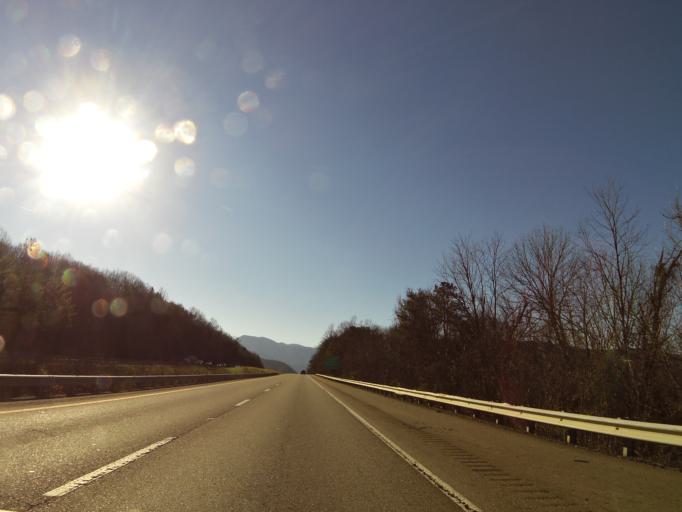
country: US
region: Tennessee
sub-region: Cocke County
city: Newport
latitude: 35.8553
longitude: -83.1840
